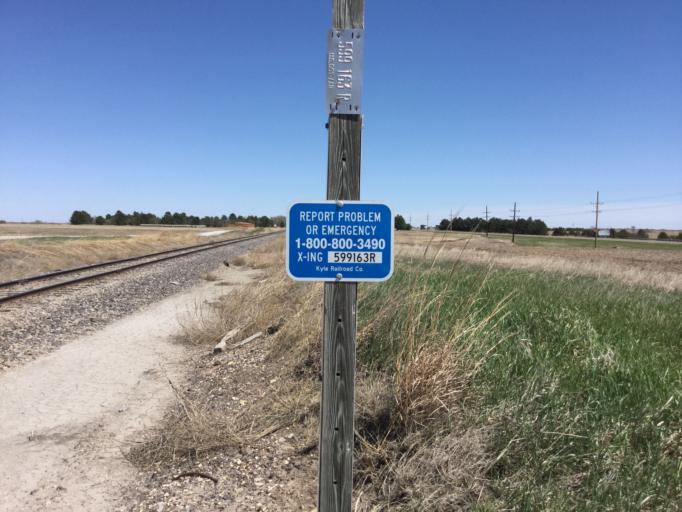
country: US
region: Kansas
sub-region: Phillips County
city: Phillipsburg
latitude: 39.7711
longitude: -99.3656
